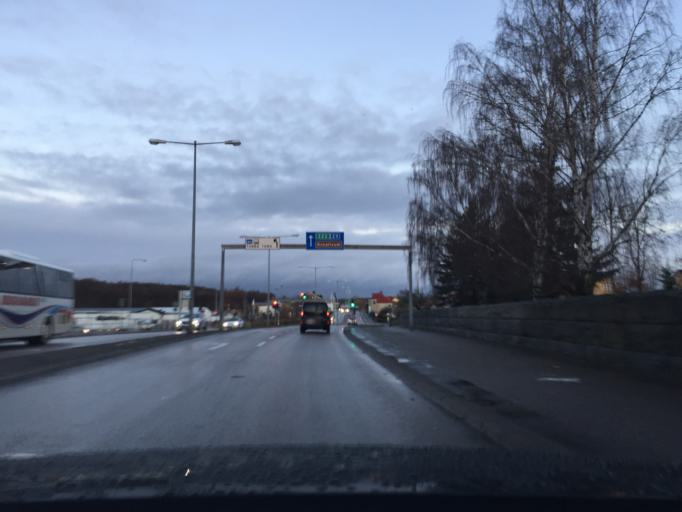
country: SE
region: Blekinge
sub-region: Karlshamns Kommun
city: Karlshamn
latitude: 56.1802
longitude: 14.8532
